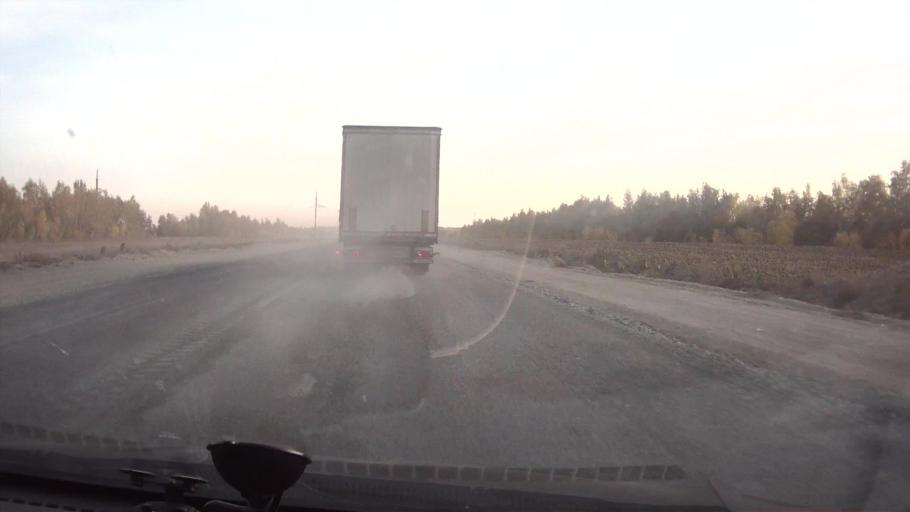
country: RU
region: Saratov
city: Kamenskiy
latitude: 50.9252
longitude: 45.5989
